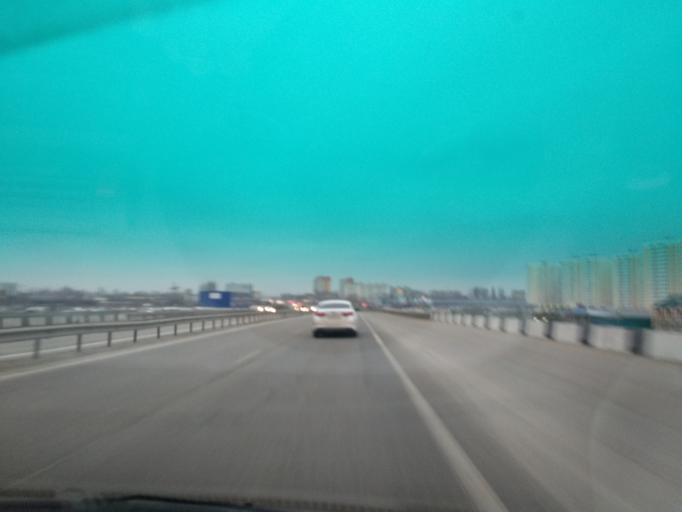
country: RU
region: Krasnodarskiy
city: Pashkovskiy
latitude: 45.0423
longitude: 39.1282
